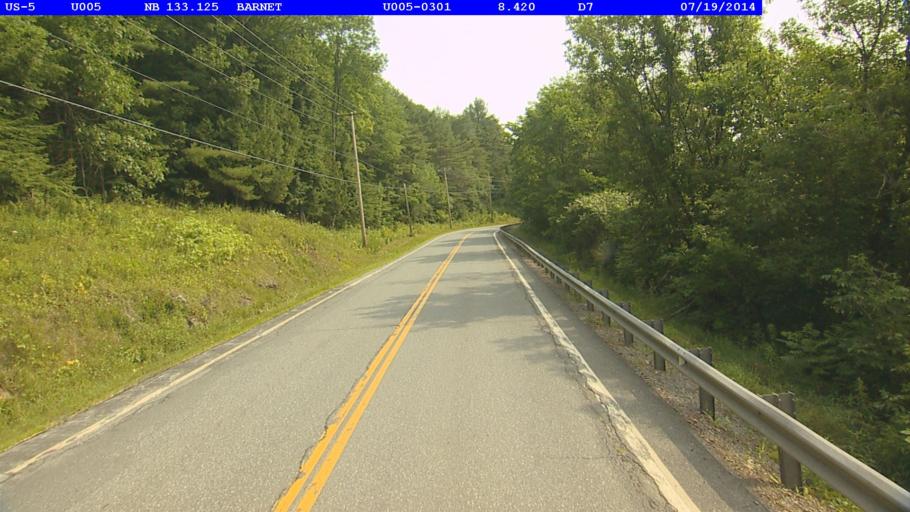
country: US
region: Vermont
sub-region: Caledonia County
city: Saint Johnsbury
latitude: 44.3638
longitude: -72.0438
